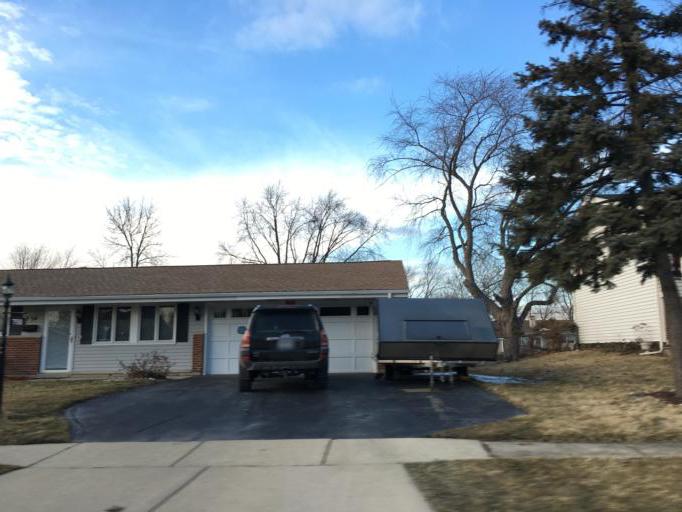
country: US
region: Illinois
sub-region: Cook County
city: Schaumburg
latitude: 42.0436
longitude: -88.0980
